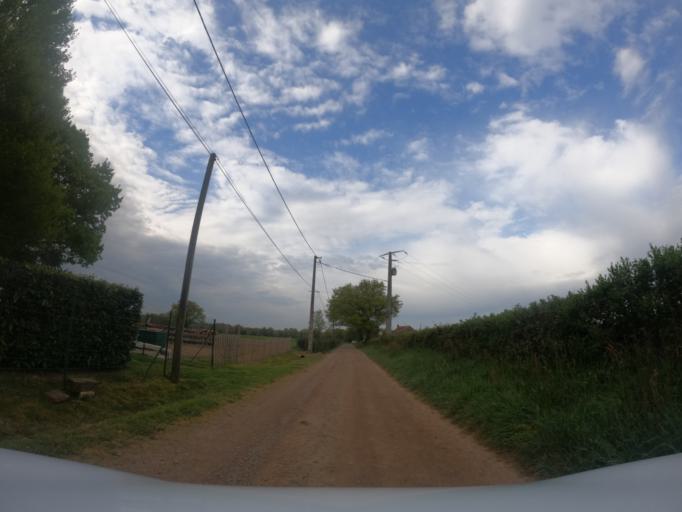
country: FR
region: Pays de la Loire
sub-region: Departement de la Vendee
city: Saint-Vincent-sur-Graon
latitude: 46.5374
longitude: -1.3749
